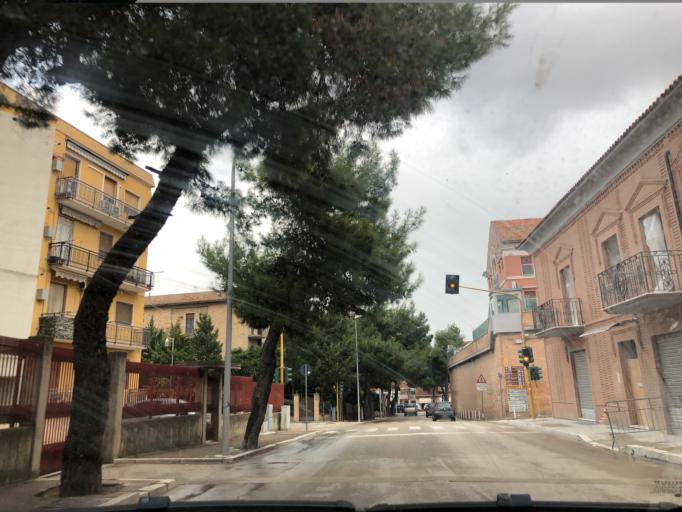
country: IT
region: Apulia
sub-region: Provincia di Foggia
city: Lucera
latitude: 41.5115
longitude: 15.3326
